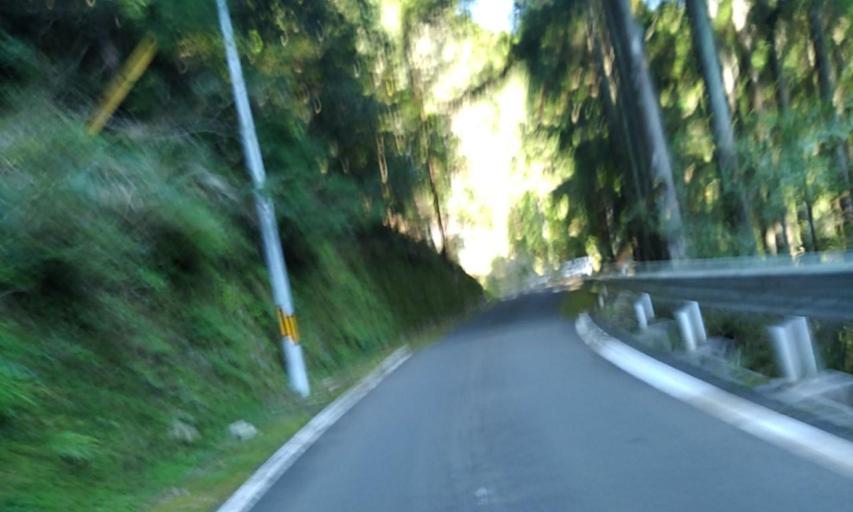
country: JP
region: Wakayama
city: Shingu
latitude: 33.9101
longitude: 135.9881
